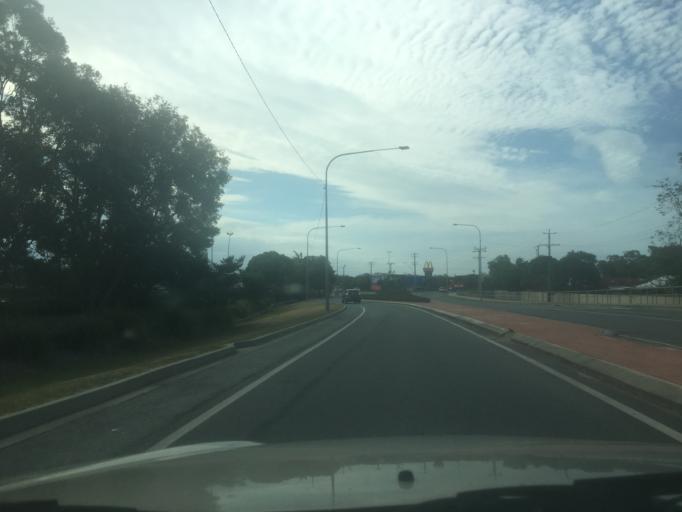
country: AU
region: Queensland
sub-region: Moreton Bay
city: Bongaree
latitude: -27.0699
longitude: 153.1616
